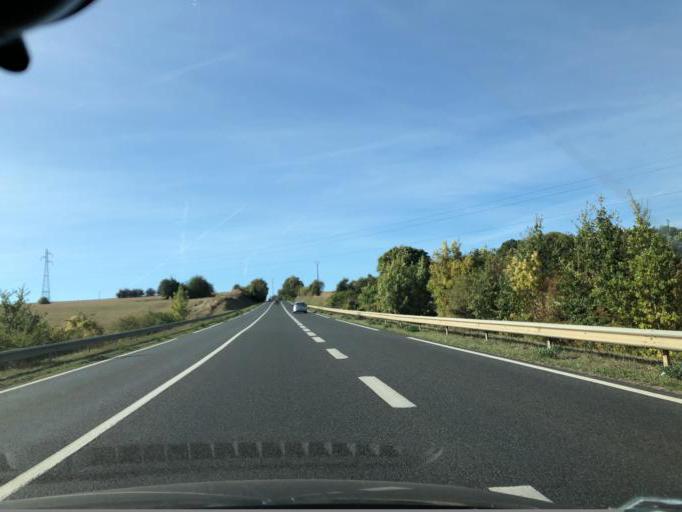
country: FR
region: Ile-de-France
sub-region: Departement de l'Essonne
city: Morigny-Champigny
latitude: 48.4315
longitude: 2.1854
